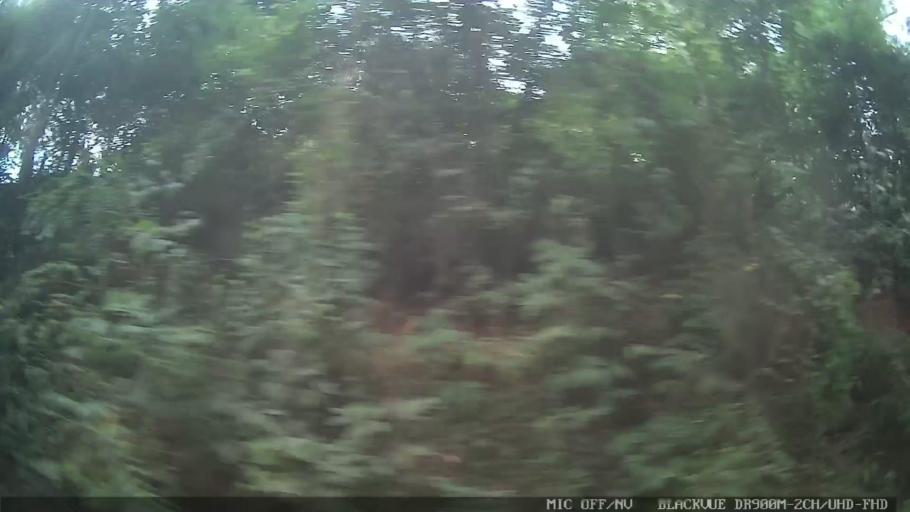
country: BR
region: Sao Paulo
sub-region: Bom Jesus Dos Perdoes
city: Bom Jesus dos Perdoes
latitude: -23.1397
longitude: -46.5040
